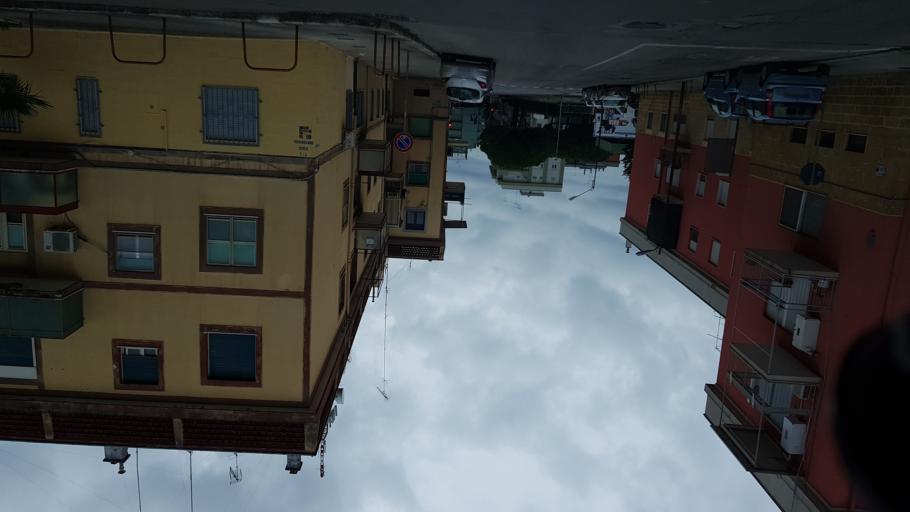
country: IT
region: Apulia
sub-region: Provincia di Brindisi
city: Brindisi
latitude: 40.6268
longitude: 17.9298
